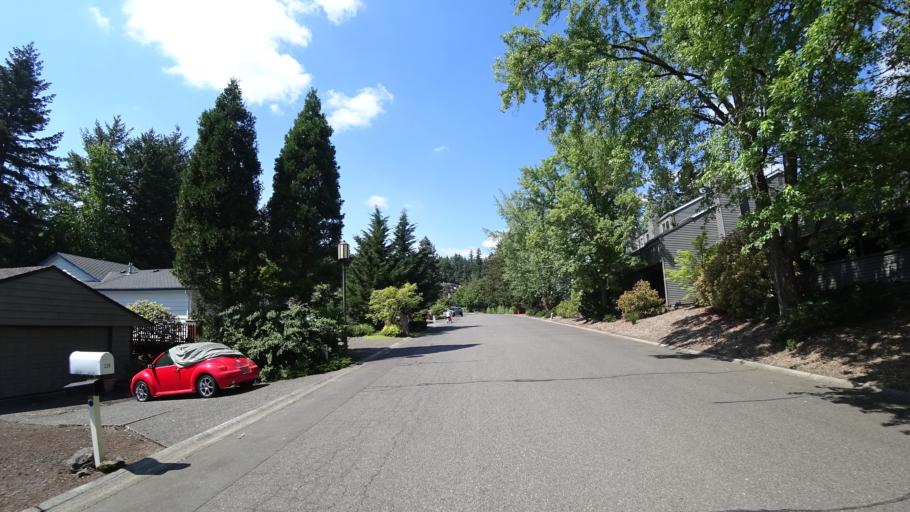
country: US
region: Oregon
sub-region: Clackamas County
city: Lake Oswego
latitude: 45.4321
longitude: -122.7067
